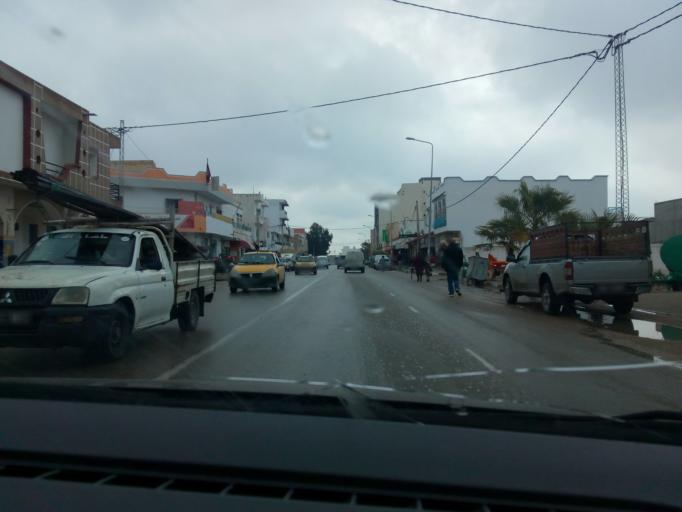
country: TN
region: Madanin
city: Medenine
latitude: 33.3554
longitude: 10.4774
